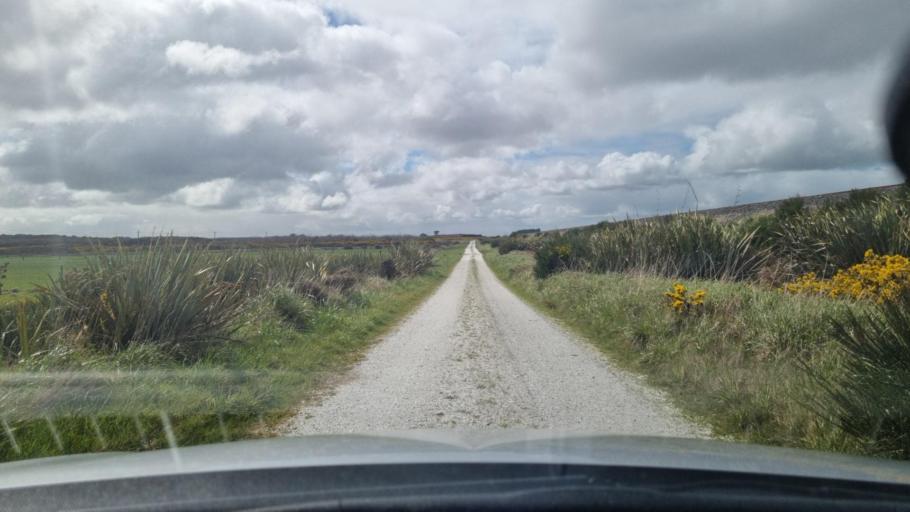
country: NZ
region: Southland
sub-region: Invercargill City
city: Bluff
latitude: -46.5348
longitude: 168.3041
